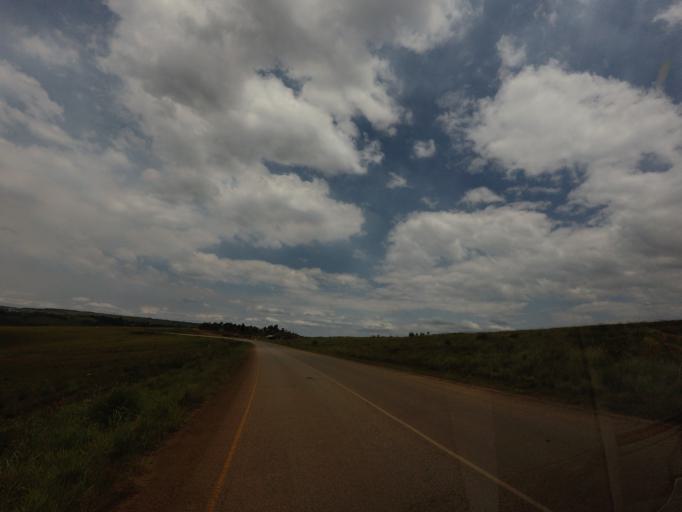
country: ZA
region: Mpumalanga
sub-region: Ehlanzeni District
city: Graksop
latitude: -24.9255
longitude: 30.8190
